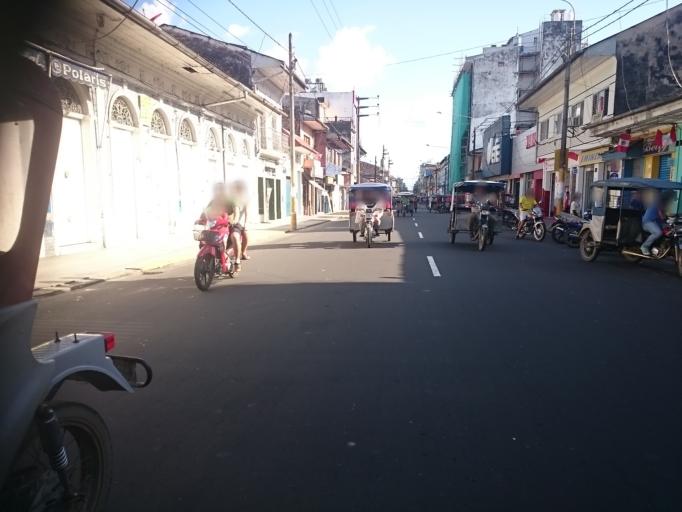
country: PE
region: Loreto
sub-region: Provincia de Maynas
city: Iquitos
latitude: -3.7521
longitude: -73.2457
